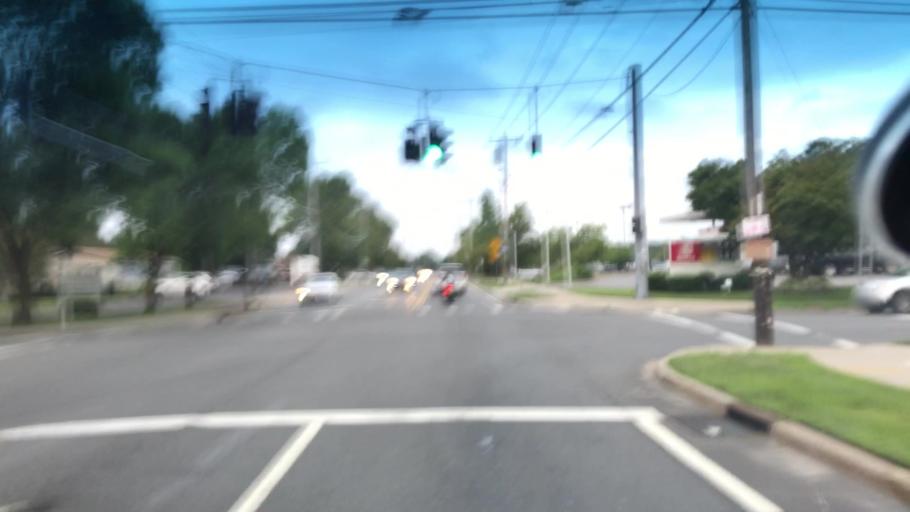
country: US
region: New York
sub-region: Suffolk County
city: Wading River
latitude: 40.9439
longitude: -72.8424
